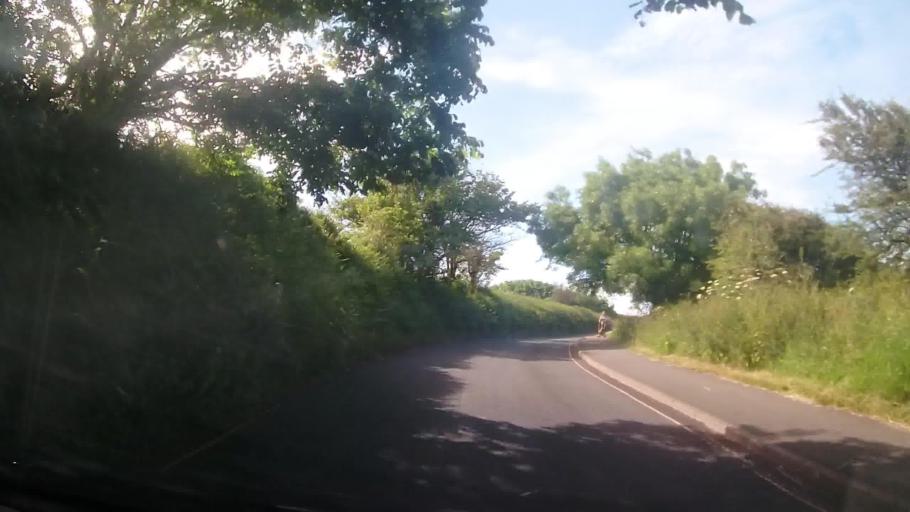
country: GB
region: England
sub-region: Devon
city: Dartmouth
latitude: 50.2879
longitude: -3.6487
